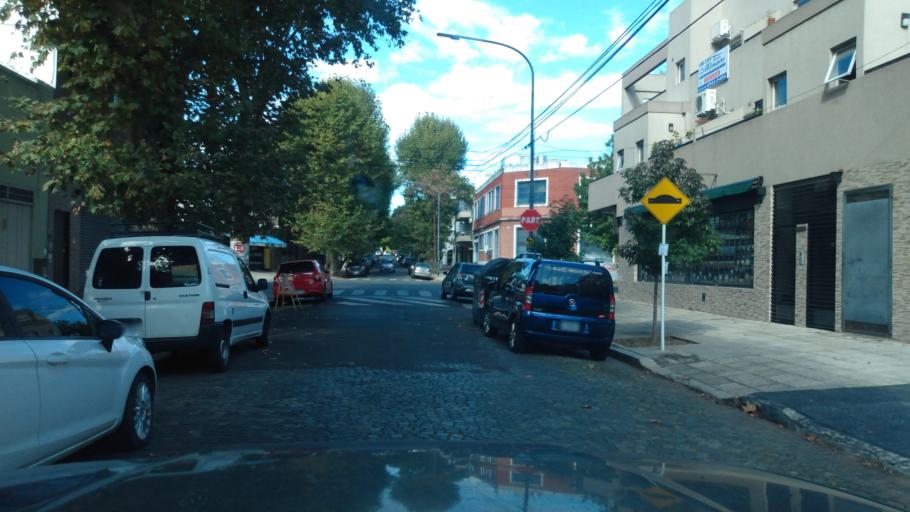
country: AR
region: Buenos Aires
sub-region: Partido de General San Martin
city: General San Martin
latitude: -34.5713
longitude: -58.4939
